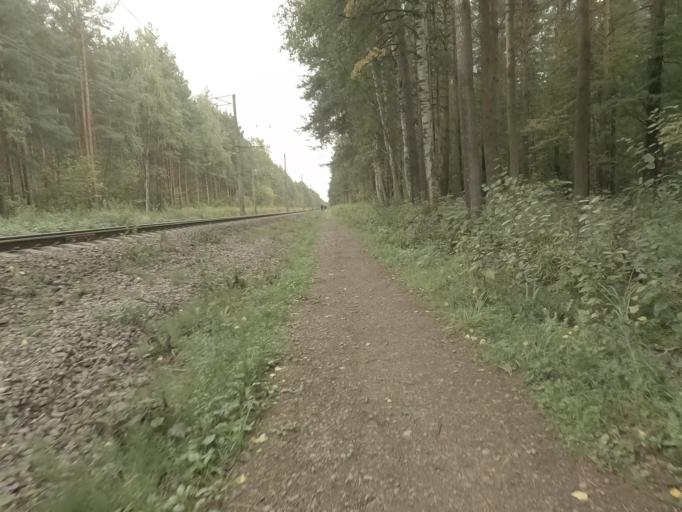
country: RU
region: St.-Petersburg
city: Krasnogvargeisky
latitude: 59.9671
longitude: 30.5122
